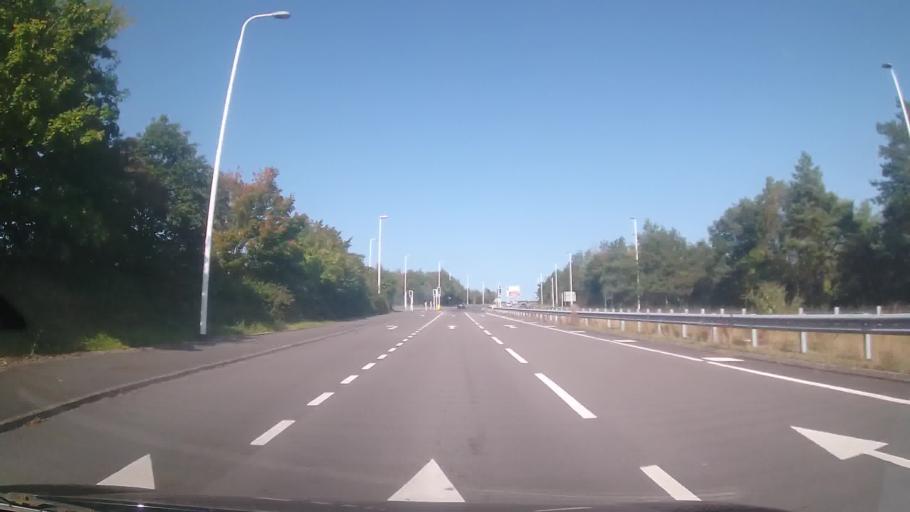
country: GB
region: Wales
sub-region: County of Ceredigion
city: Cardigan
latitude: 52.0887
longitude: -4.6457
